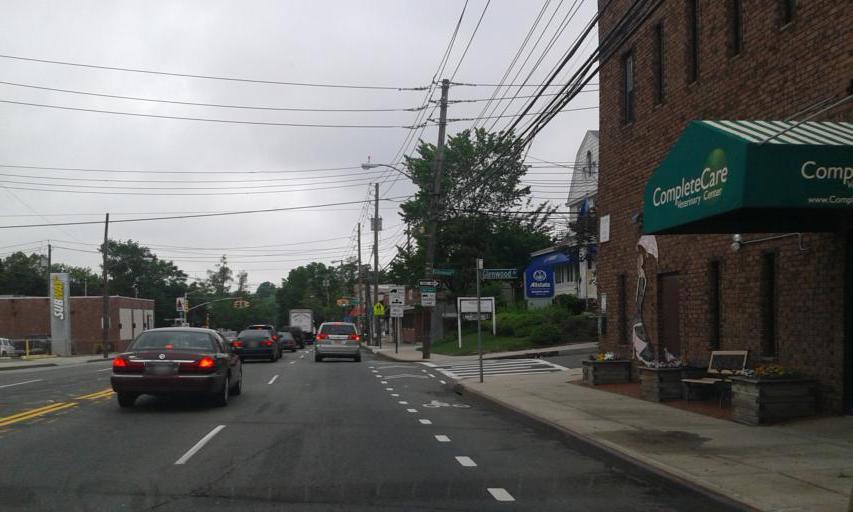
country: US
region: New Jersey
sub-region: Hudson County
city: Bayonne
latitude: 40.6155
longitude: -74.1027
